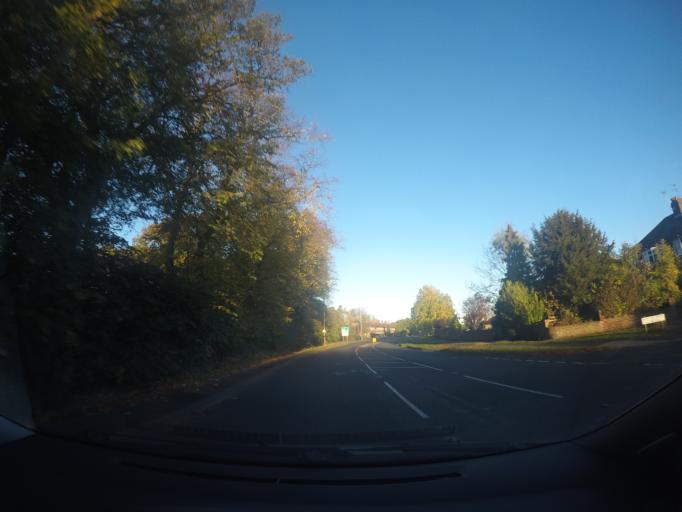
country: GB
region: England
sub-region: City of York
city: Skelton
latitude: 53.9799
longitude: -1.1141
